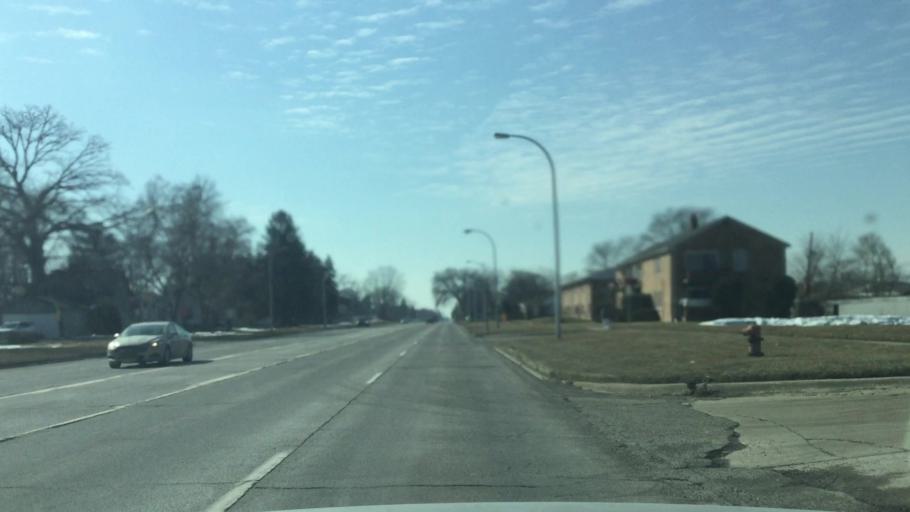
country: US
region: Michigan
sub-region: Wayne County
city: Inkster
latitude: 42.3117
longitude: -83.3141
